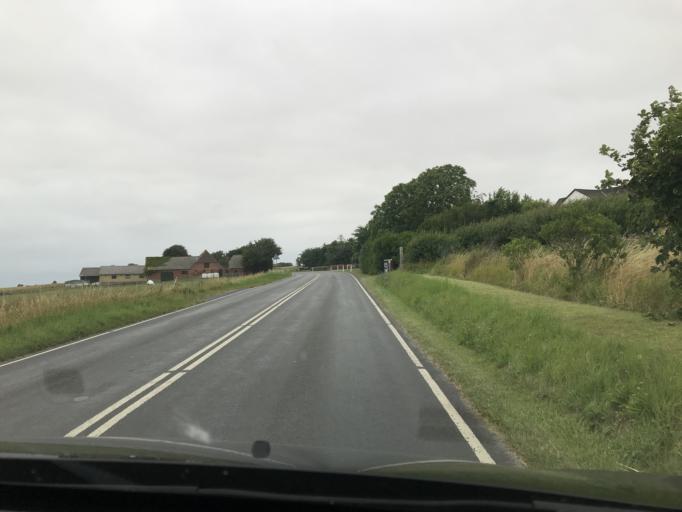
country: DK
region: South Denmark
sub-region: AEro Kommune
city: AEroskobing
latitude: 54.8445
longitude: 10.4319
